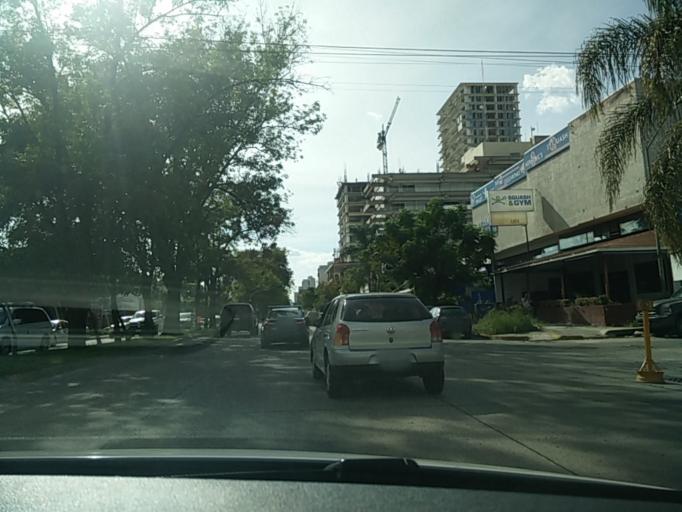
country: MX
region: Jalisco
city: Guadalajara
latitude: 20.6795
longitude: -103.3805
